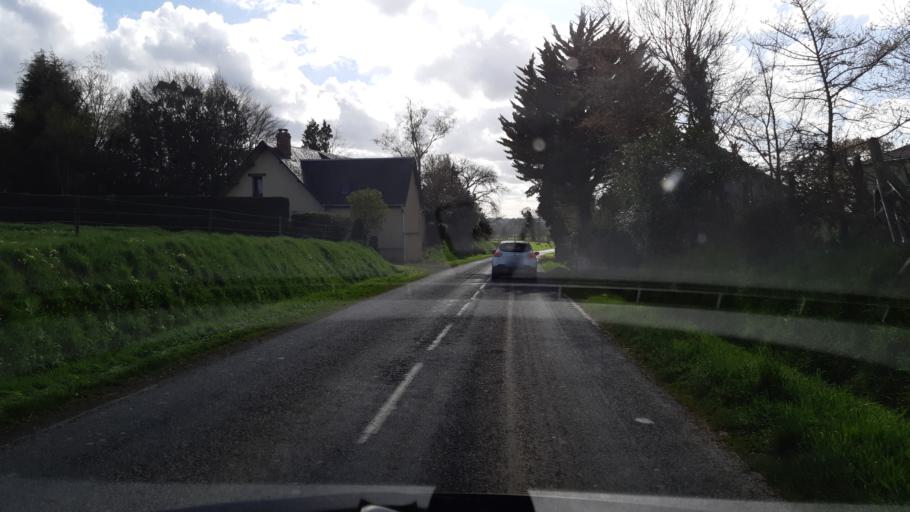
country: FR
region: Lower Normandy
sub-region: Departement de la Manche
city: Percy
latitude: 49.0147
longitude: -1.1661
